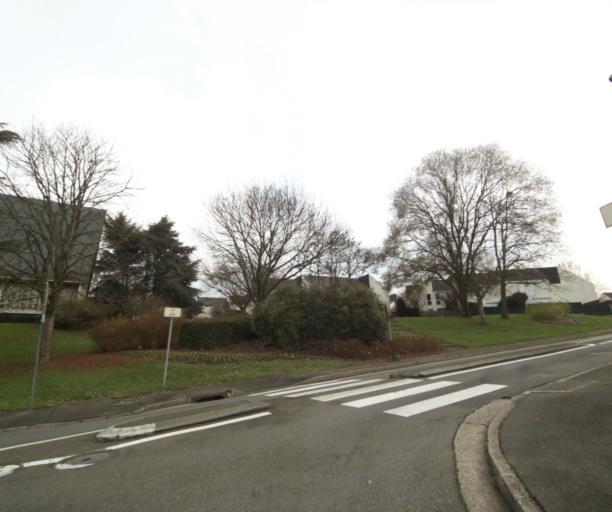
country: FR
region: Pays de la Loire
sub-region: Departement de la Sarthe
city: Coulaines
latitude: 48.0183
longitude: 0.2087
